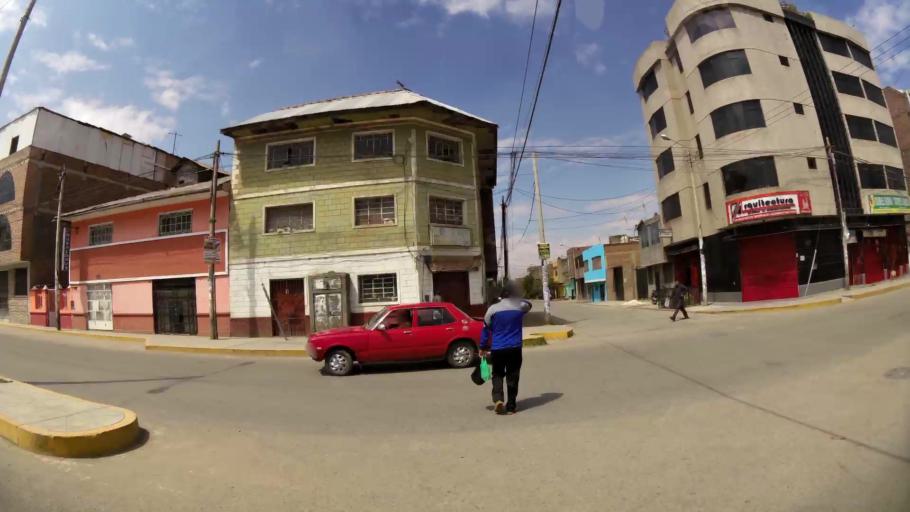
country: PE
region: Junin
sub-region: Provincia de Huancayo
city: Huancayo
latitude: -12.0831
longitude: -75.2033
